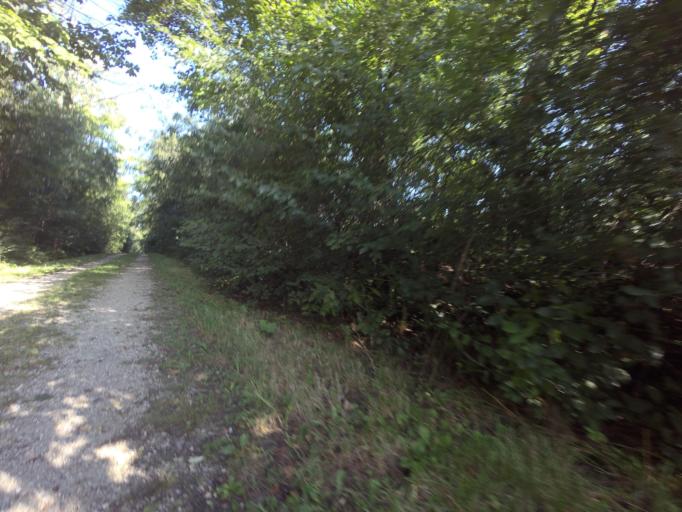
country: CA
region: Ontario
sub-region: Wellington County
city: Guelph
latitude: 43.6534
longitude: -80.4196
